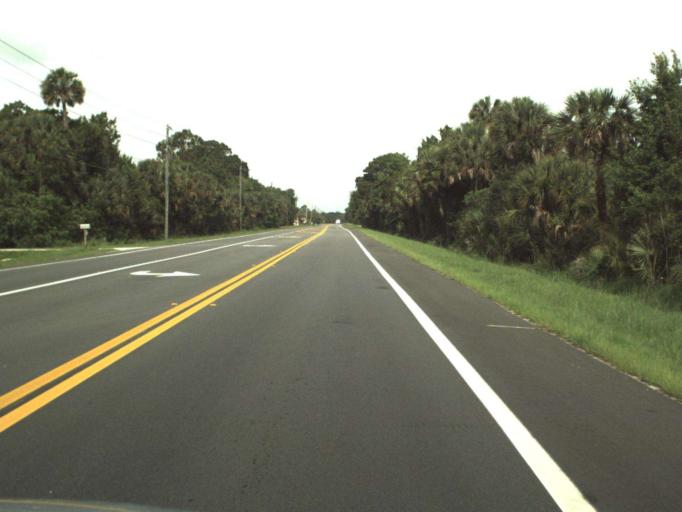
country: US
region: Florida
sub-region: Seminole County
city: Geneva
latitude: 28.7168
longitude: -81.0578
